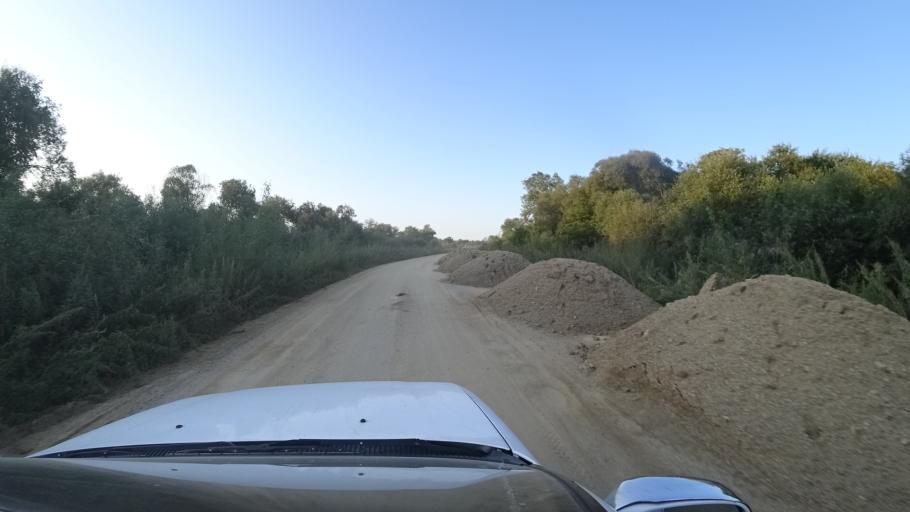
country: RU
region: Primorskiy
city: Dal'nerechensk
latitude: 45.9383
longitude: 133.7601
